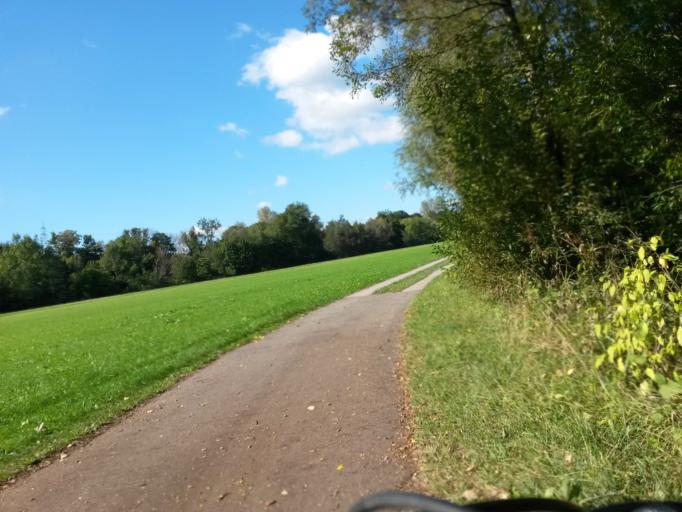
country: DE
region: Baden-Wuerttemberg
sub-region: Regierungsbezirk Stuttgart
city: Markgroningen
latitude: 48.9291
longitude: 9.0758
